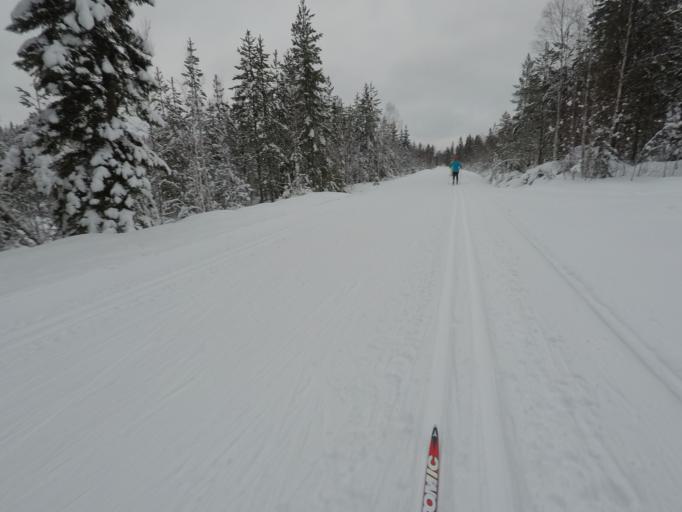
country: SE
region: Dalarna
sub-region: Ludvika Kommun
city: Abborrberget
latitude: 60.1381
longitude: 14.4843
